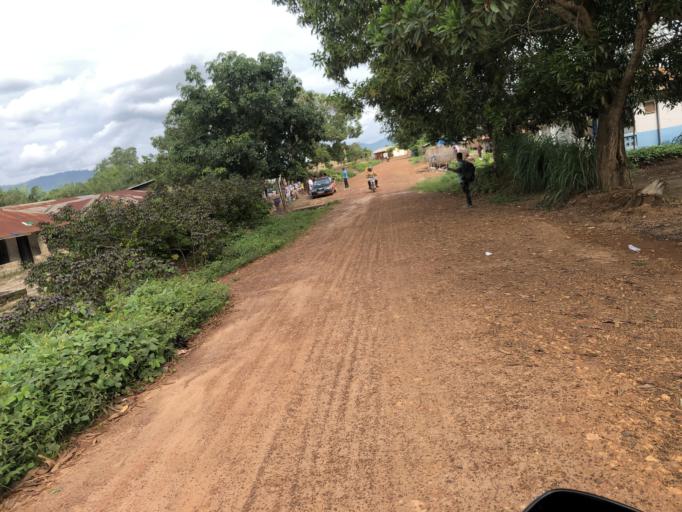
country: SL
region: Northern Province
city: Masaka
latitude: 8.7493
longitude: -11.8426
